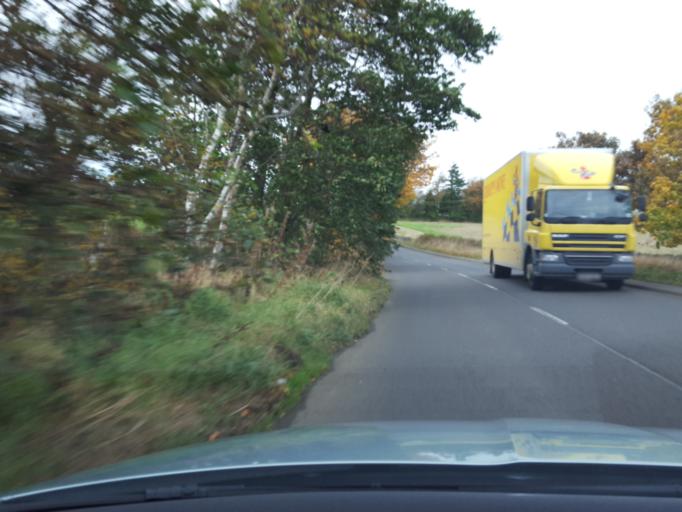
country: GB
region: Scotland
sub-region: Edinburgh
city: Ratho
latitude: 55.9191
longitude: -3.3779
